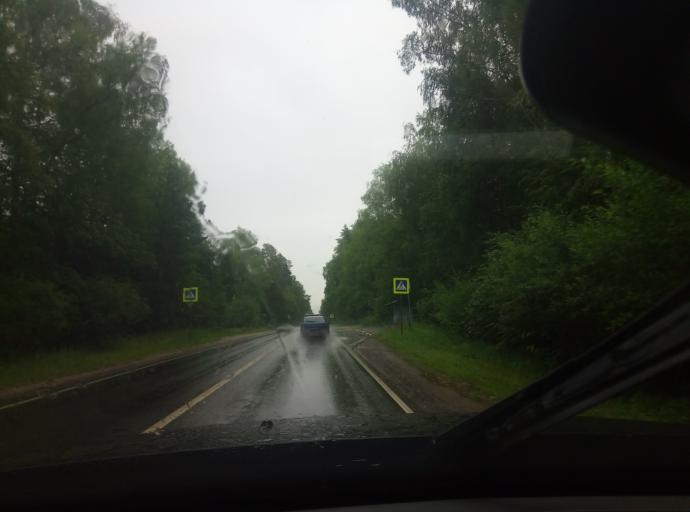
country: RU
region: Moskovskaya
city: Protvino
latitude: 54.8864
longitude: 37.1836
